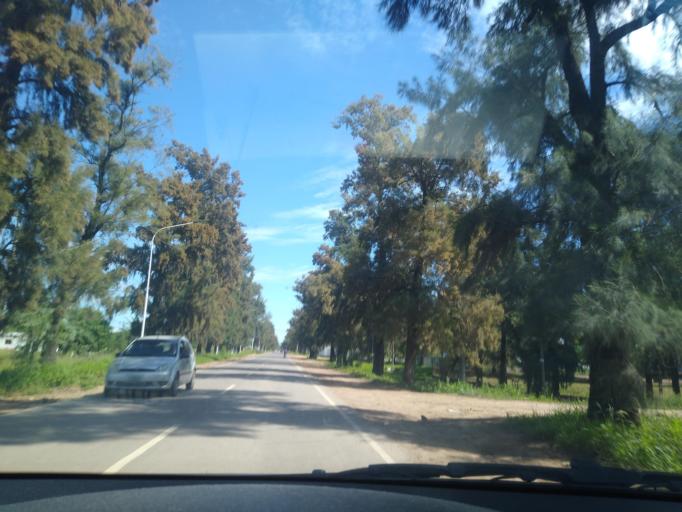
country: AR
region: Chaco
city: Presidencia Roque Saenz Pena
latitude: -26.7735
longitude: -60.4165
